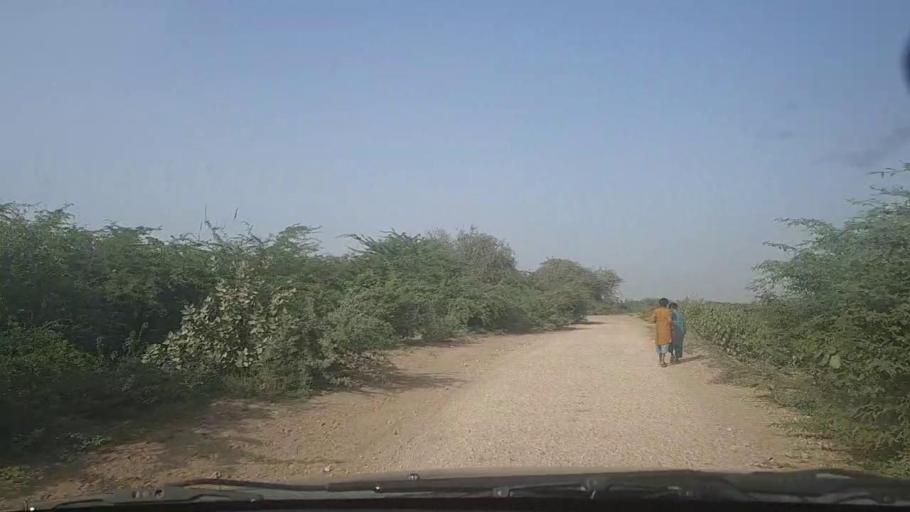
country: PK
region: Sindh
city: Keti Bandar
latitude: 24.2648
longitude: 67.5666
